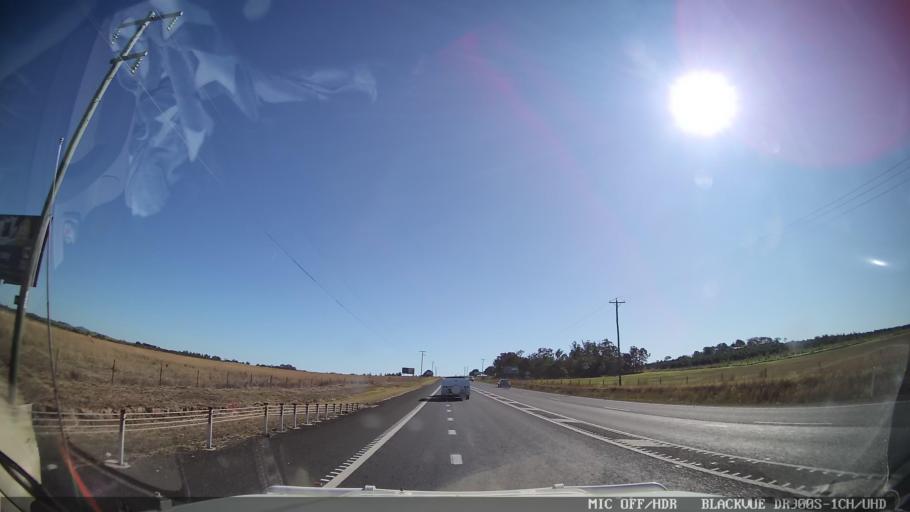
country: AU
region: Queensland
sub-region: Bundaberg
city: Childers
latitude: -25.2481
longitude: 152.3315
